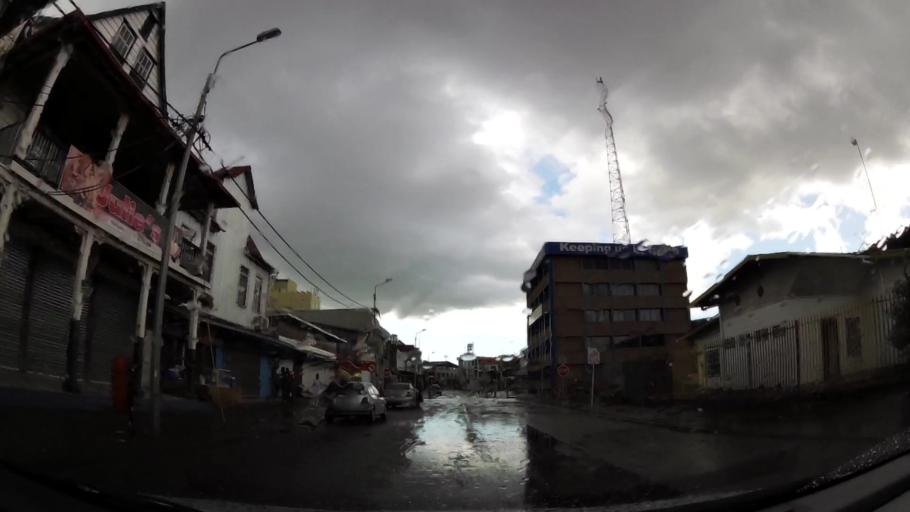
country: SR
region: Paramaribo
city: Paramaribo
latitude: 5.8255
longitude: -55.1570
